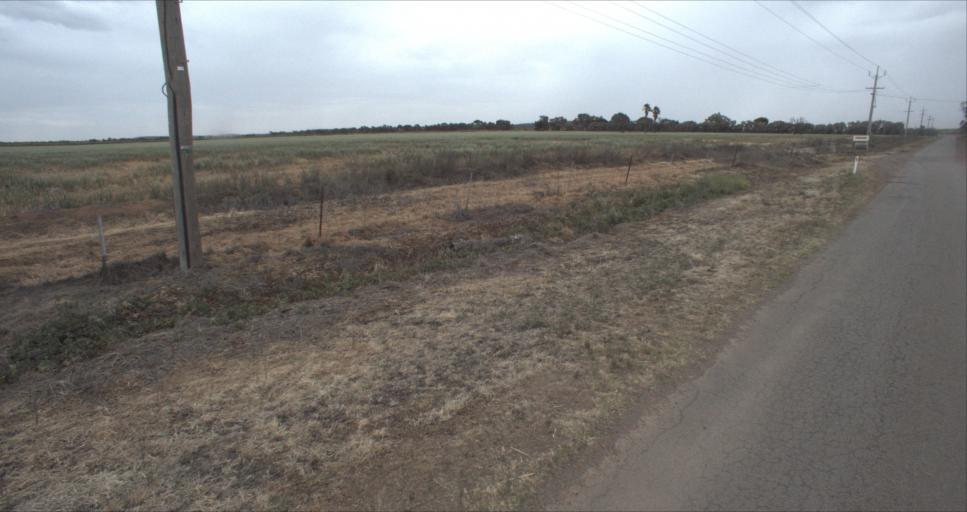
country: AU
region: New South Wales
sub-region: Leeton
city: Leeton
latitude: -34.4073
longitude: 146.3410
